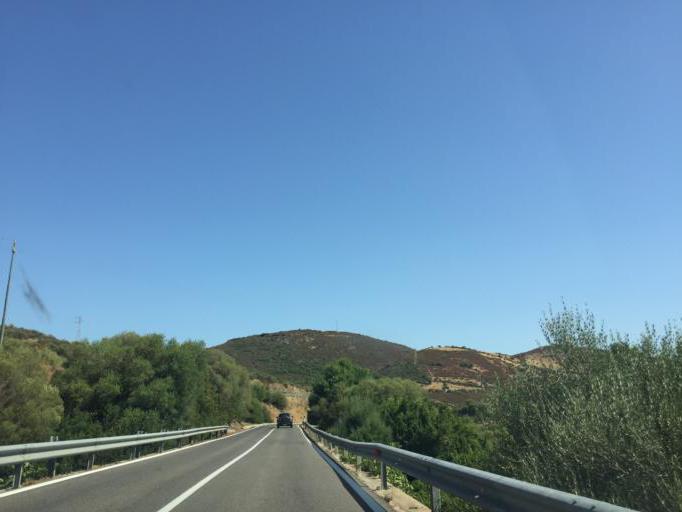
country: IT
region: Sardinia
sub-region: Provincia di Olbia-Tempio
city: San Teodoro
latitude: 40.7338
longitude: 9.6483
